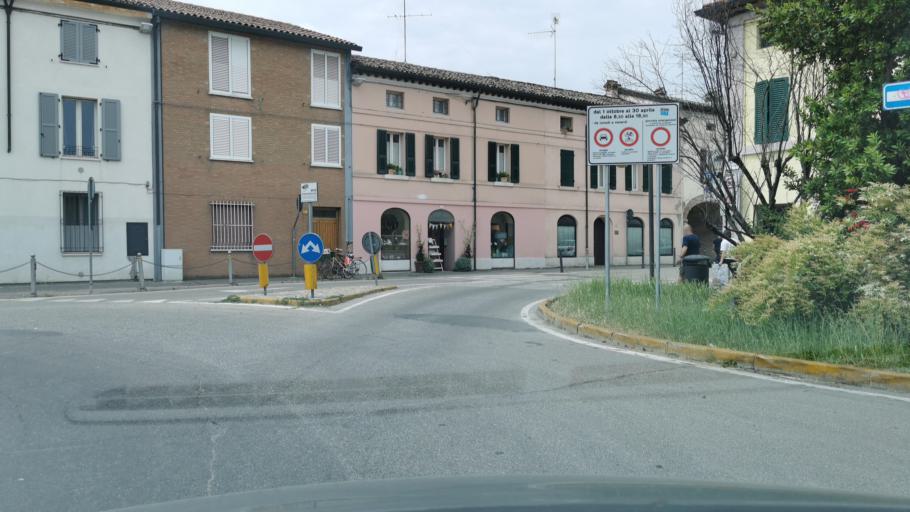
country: IT
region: Emilia-Romagna
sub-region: Provincia di Ravenna
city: Bagnacavallo
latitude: 44.4156
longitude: 11.9801
